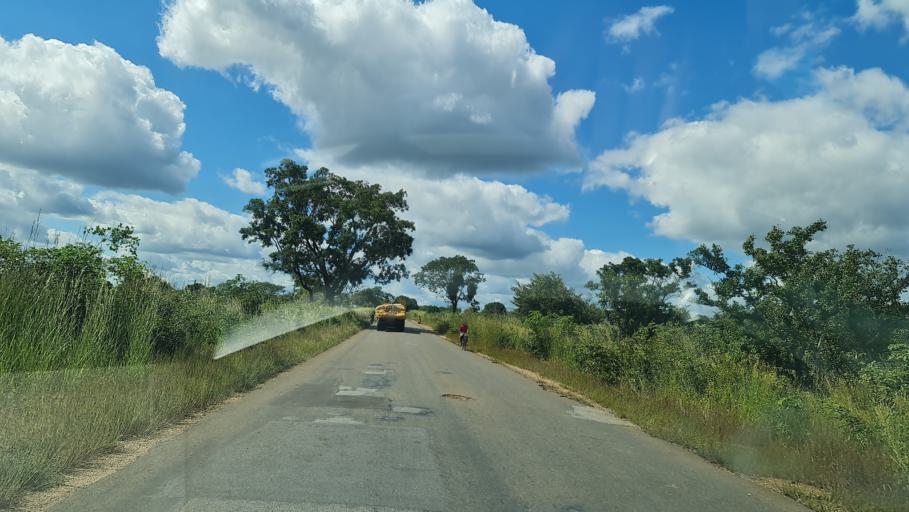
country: MZ
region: Zambezia
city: Quelimane
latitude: -17.5126
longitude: 36.2258
